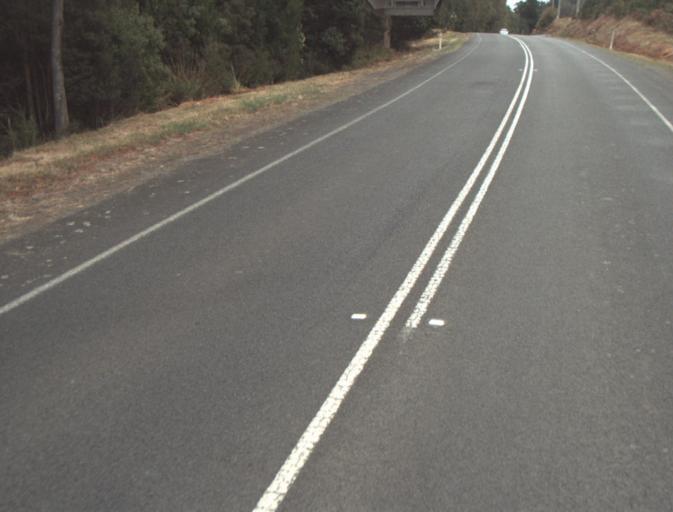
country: AU
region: Tasmania
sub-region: Launceston
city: Mayfield
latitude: -41.2761
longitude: 147.2193
